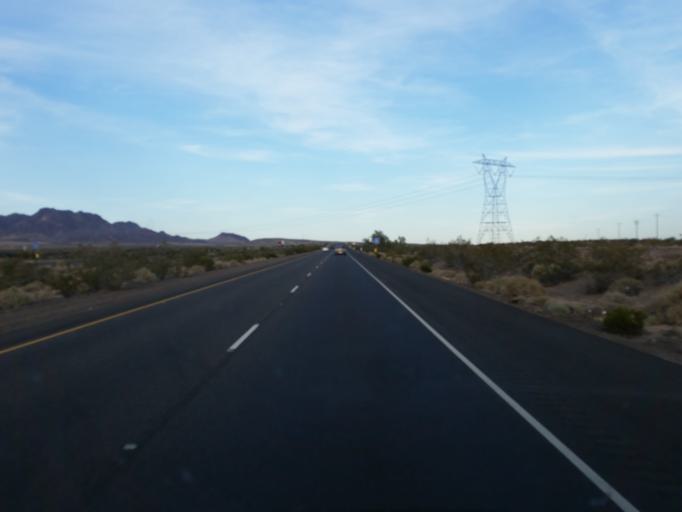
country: US
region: California
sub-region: San Bernardino County
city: Fort Irwin
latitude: 34.7747
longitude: -116.3781
